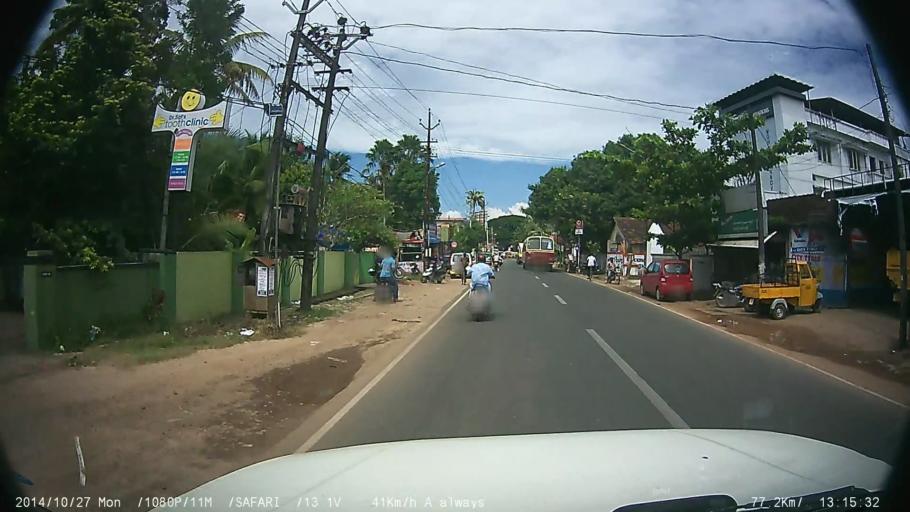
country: IN
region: Kerala
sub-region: Alappuzha
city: Alleppey
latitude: 9.4869
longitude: 76.3380
